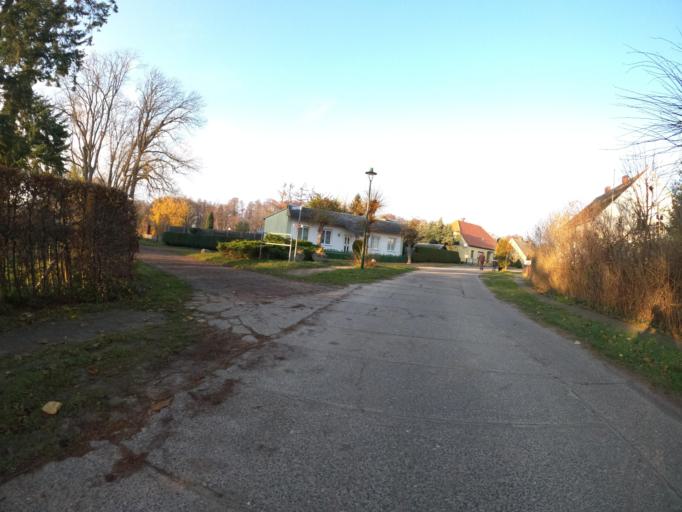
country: PL
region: West Pomeranian Voivodeship
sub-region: Powiat policki
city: Nowe Warpno
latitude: 53.6914
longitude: 14.2551
